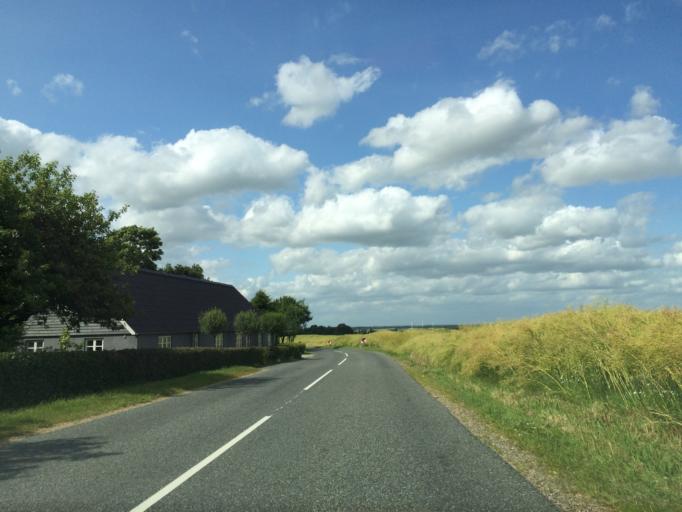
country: DK
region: Central Jutland
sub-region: Skanderborg Kommune
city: Ry
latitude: 56.2052
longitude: 9.7549
